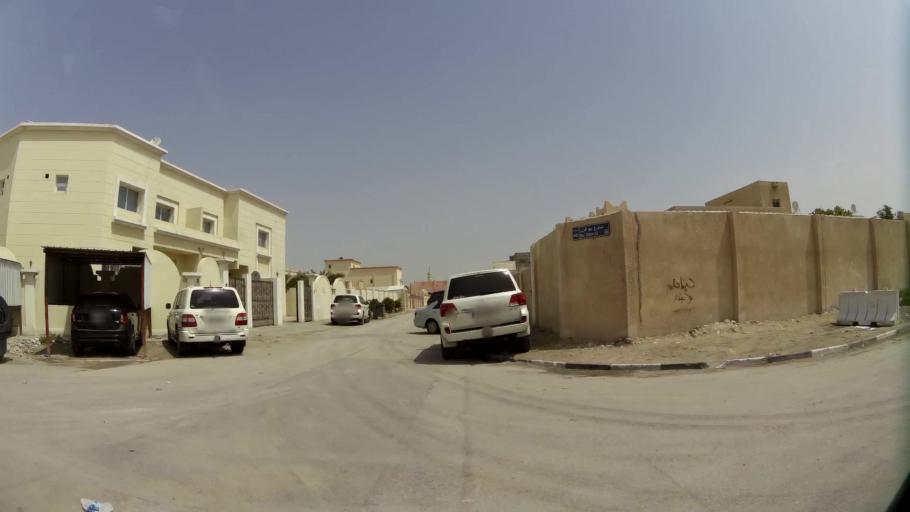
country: QA
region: Baladiyat ar Rayyan
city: Ar Rayyan
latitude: 25.2360
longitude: 51.4161
